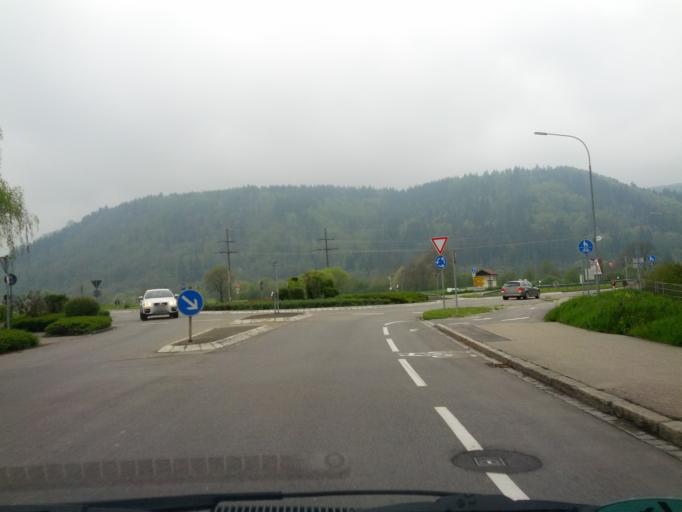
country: DE
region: Baden-Wuerttemberg
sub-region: Freiburg Region
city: Maulburg
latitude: 47.6485
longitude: 7.8012
